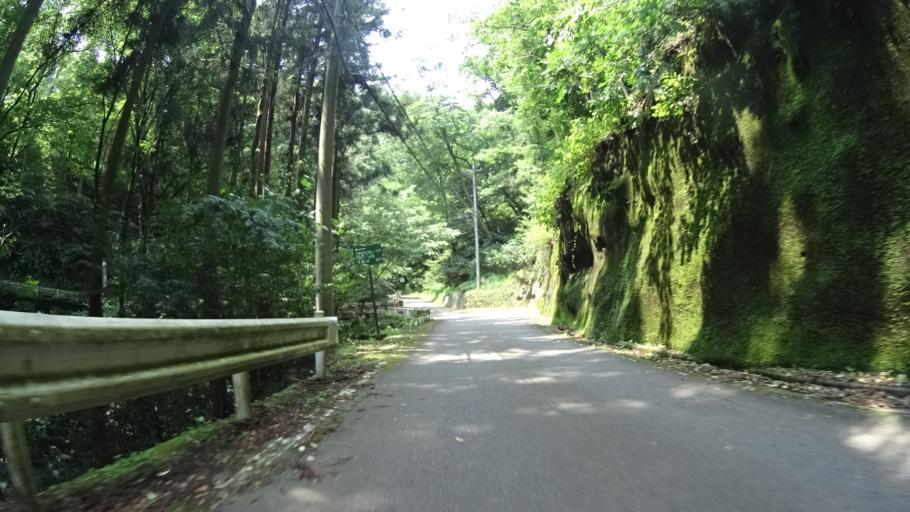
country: JP
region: Gunma
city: Tomioka
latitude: 36.0821
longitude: 138.7104
